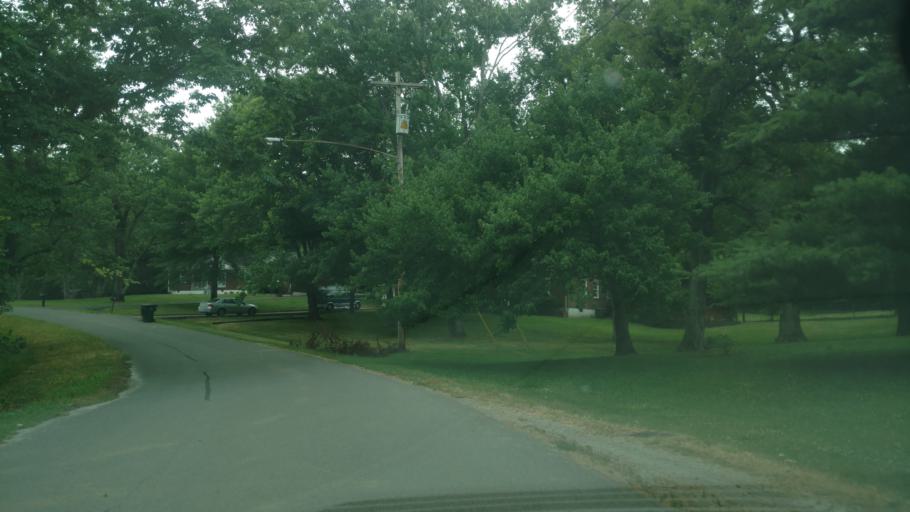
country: US
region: Tennessee
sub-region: Davidson County
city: Nashville
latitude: 36.1945
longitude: -86.7210
